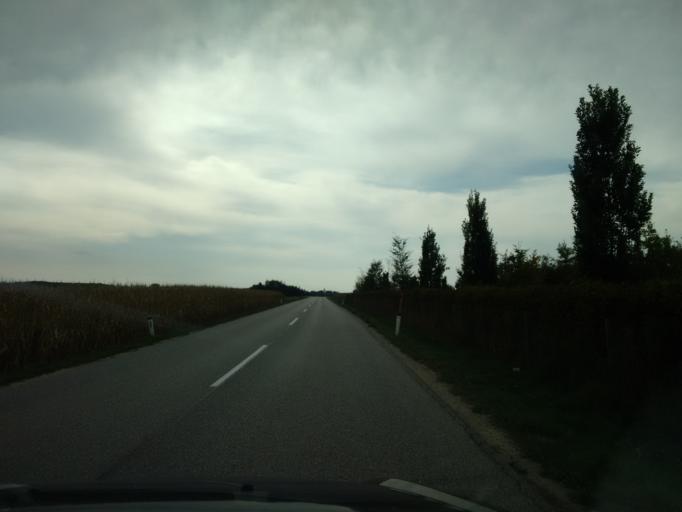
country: AT
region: Upper Austria
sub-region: Wels-Land
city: Marchtrenk
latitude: 48.1569
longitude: 14.1355
